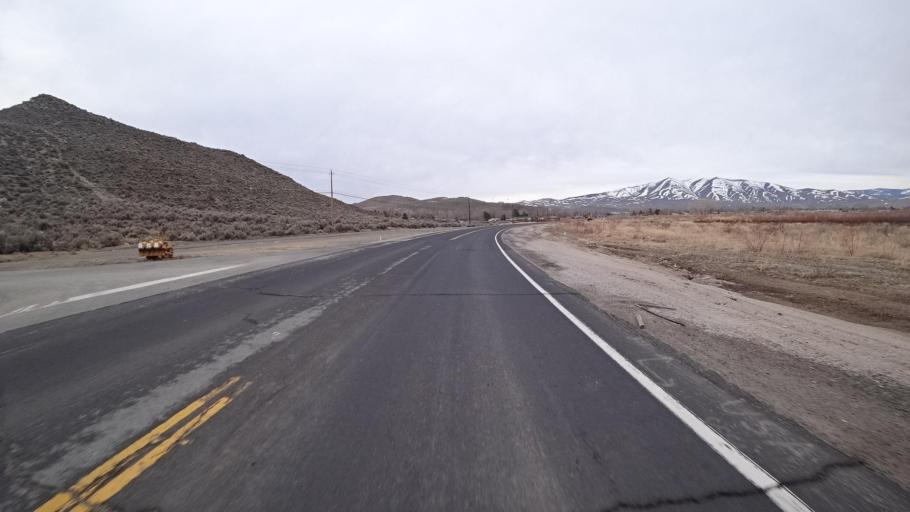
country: US
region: Nevada
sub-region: Washoe County
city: Lemmon Valley
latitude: 39.6488
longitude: -119.8282
